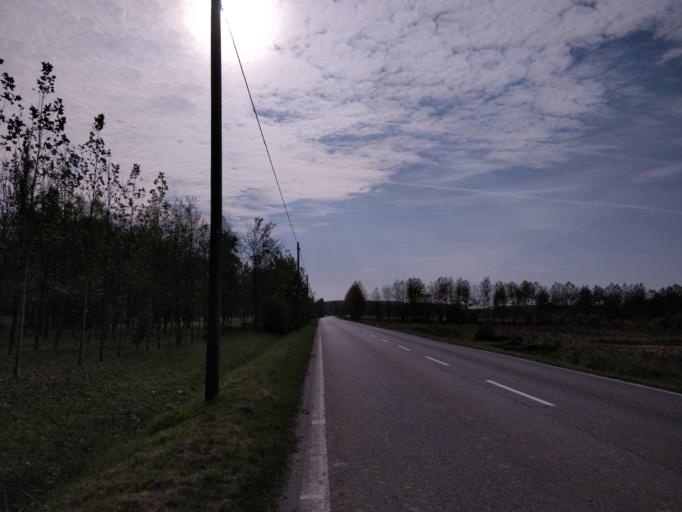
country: IT
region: Friuli Venezia Giulia
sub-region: Provincia di Udine
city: Bertiolo
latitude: 45.9199
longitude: 13.0481
